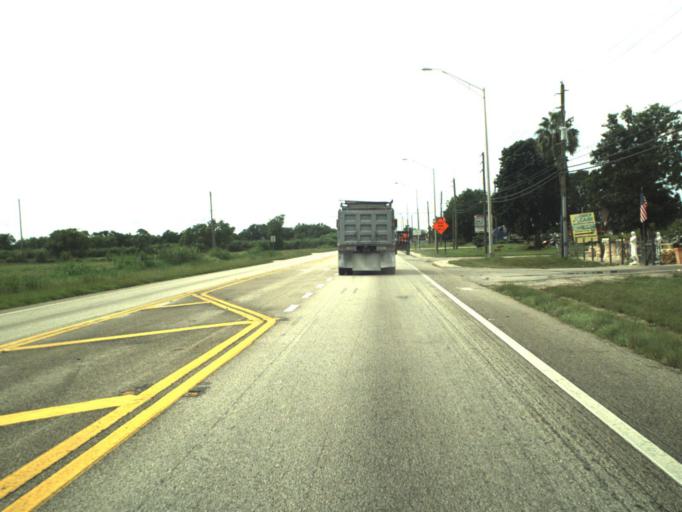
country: US
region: Florida
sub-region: Miami-Dade County
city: Richmond West
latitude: 25.5886
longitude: -80.4785
